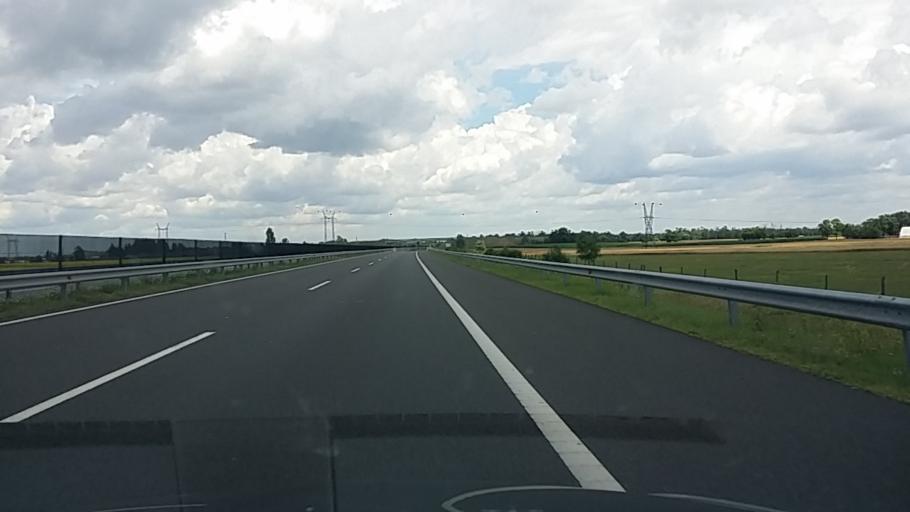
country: HU
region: Hajdu-Bihar
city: Hajdunanas
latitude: 47.8575
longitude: 21.3575
